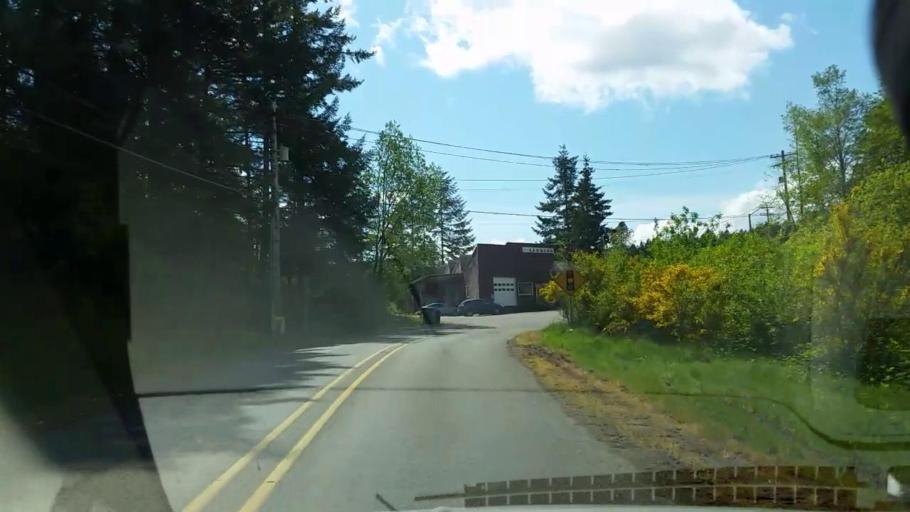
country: US
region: Washington
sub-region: Pierce County
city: Key Center
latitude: 47.3411
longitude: -122.7438
